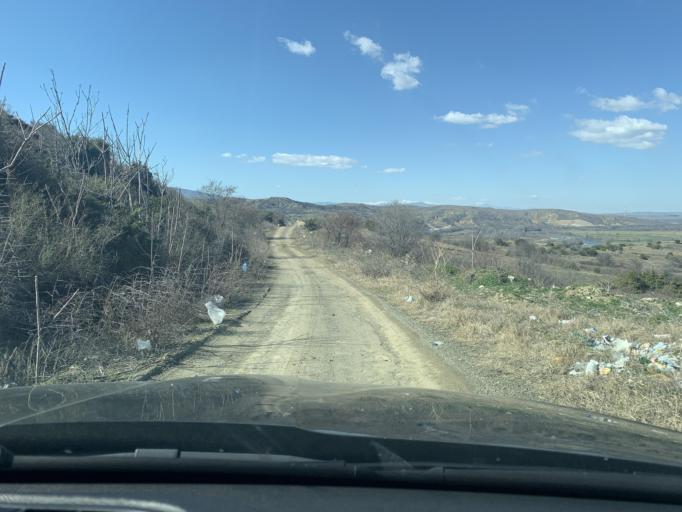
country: MK
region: Demir Kapija
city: Demir Kapija
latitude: 41.4144
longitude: 22.2135
